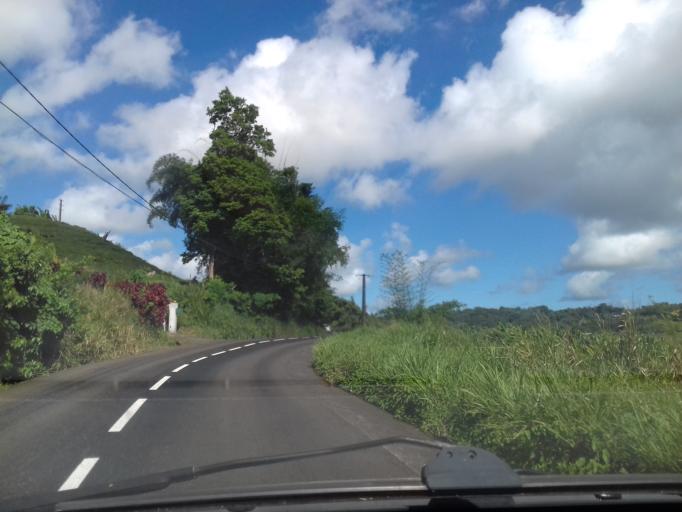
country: MQ
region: Martinique
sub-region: Martinique
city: Le Gros-Morne
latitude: 14.6853
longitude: -61.0156
